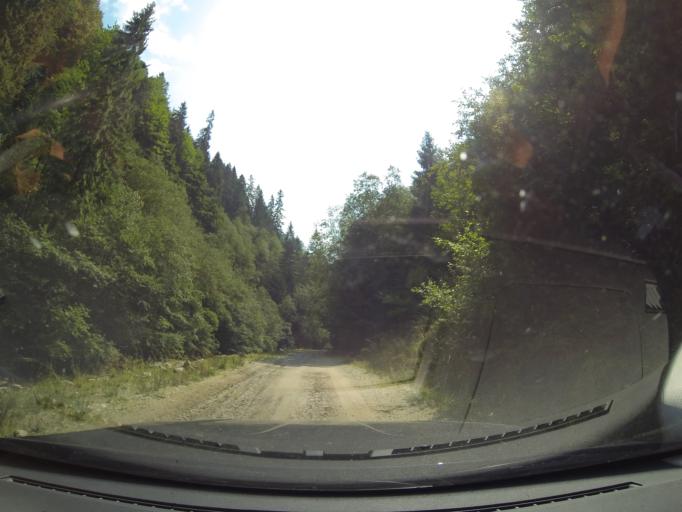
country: RO
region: Arges
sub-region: Comuna Arefu
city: Arefu
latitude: 45.4889
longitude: 24.6368
